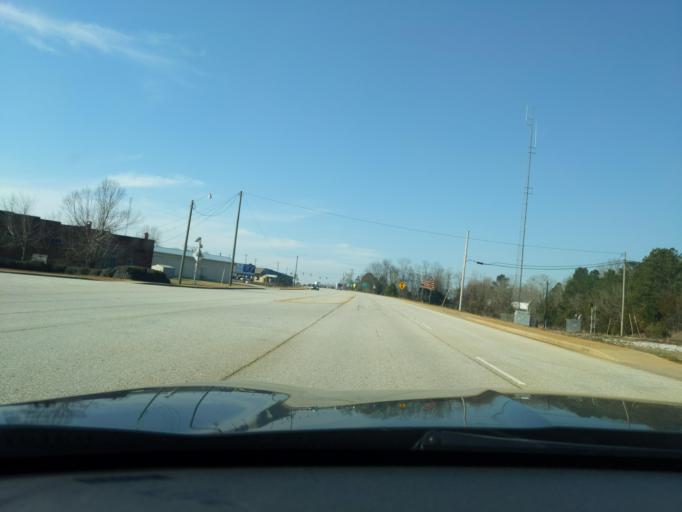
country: US
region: South Carolina
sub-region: Abbeville County
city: Calhoun Falls
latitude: 34.0933
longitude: -82.5952
